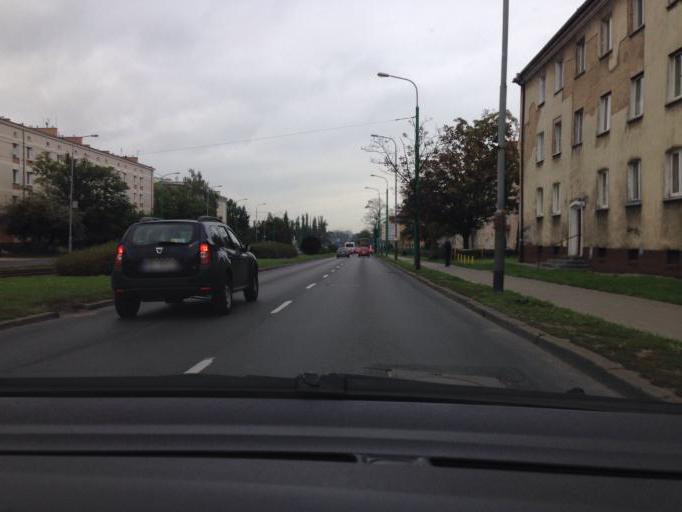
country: PL
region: Greater Poland Voivodeship
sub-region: Poznan
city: Poznan
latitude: 52.4128
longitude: 16.8903
